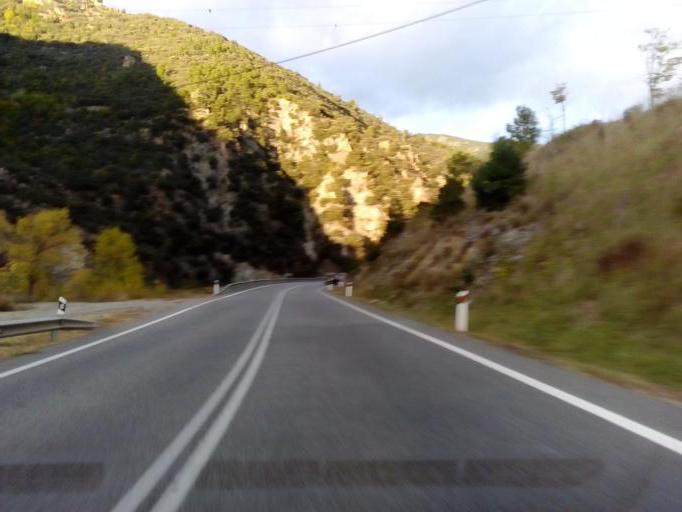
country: ES
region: Catalonia
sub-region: Provincia de Lleida
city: Toloriu
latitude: 42.3713
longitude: 1.6200
